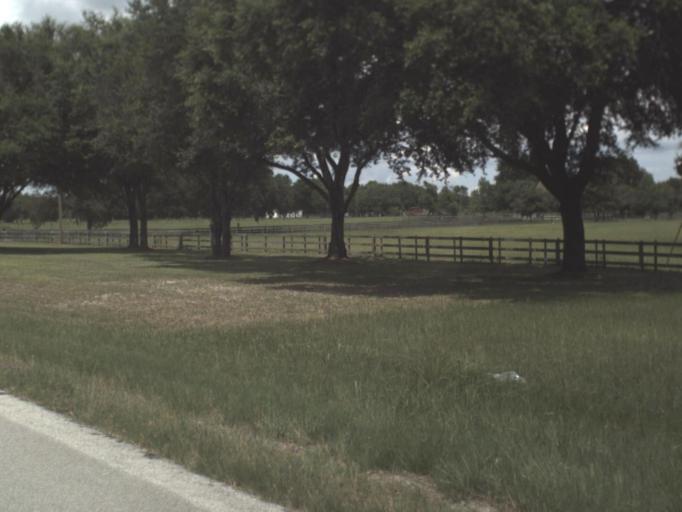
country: US
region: Florida
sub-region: Alachua County
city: High Springs
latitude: 29.7496
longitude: -82.6073
